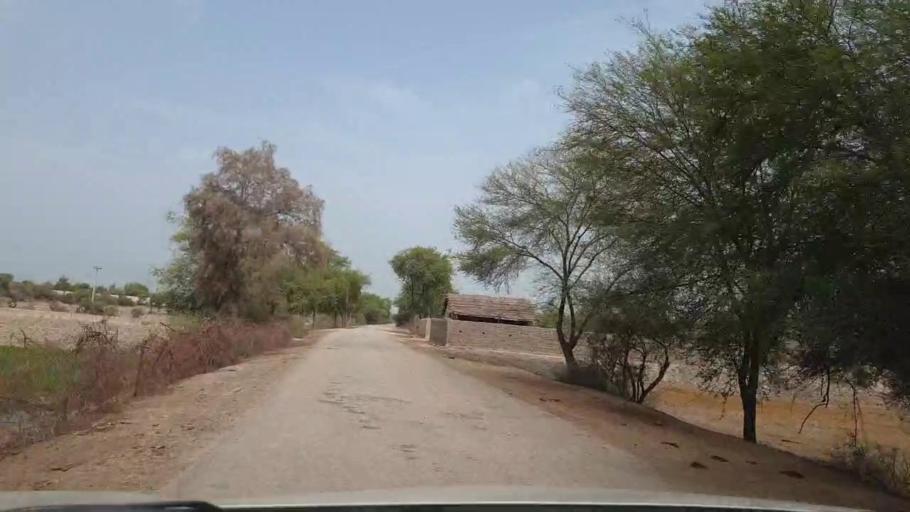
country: PK
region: Sindh
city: Dokri
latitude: 27.4039
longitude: 68.2465
